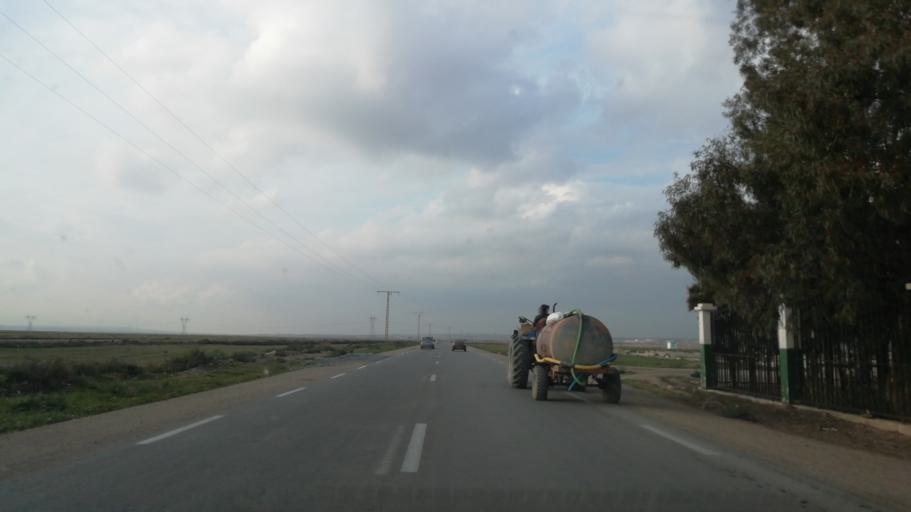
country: DZ
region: Mascara
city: Sig
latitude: 35.6962
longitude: -0.0220
